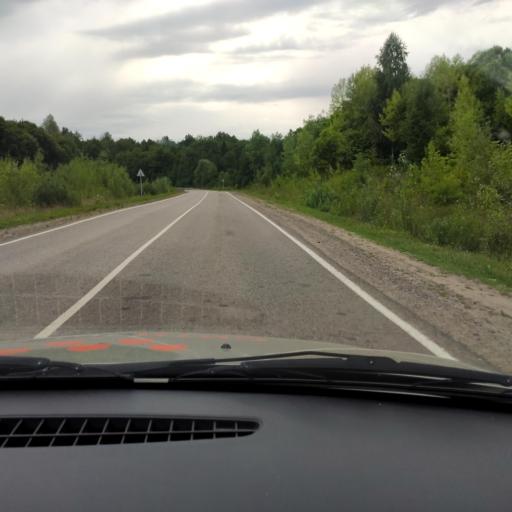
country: RU
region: Bashkortostan
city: Krasnaya Gorka
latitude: 55.2800
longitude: 56.7033
